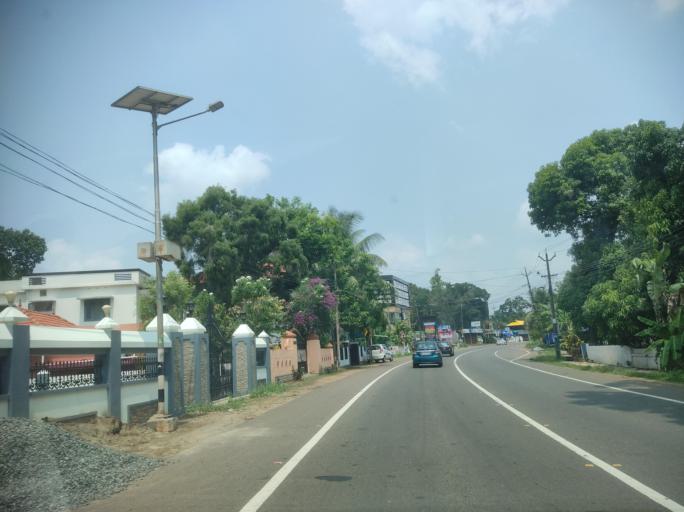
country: IN
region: Kerala
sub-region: Pattanamtitta
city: Tiruvalla
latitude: 9.4100
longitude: 76.5553
